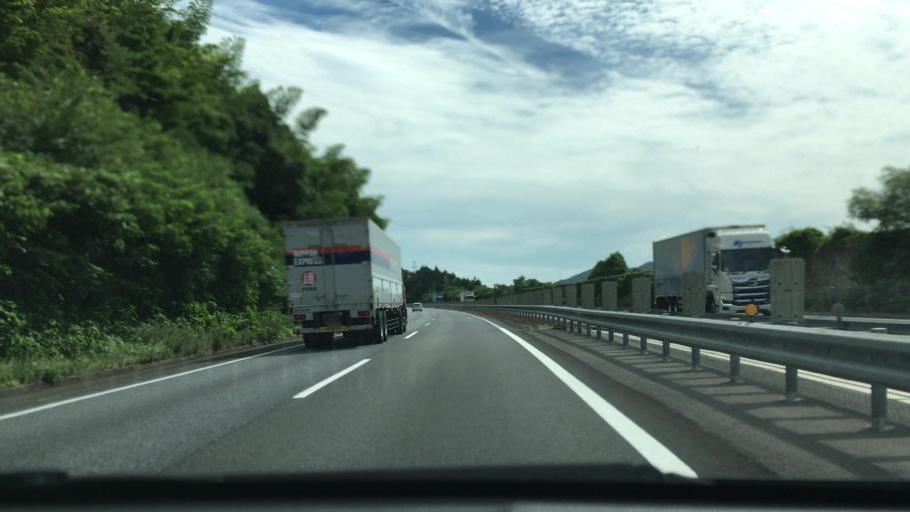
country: JP
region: Yamaguchi
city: Ogori-shimogo
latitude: 34.1298
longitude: 131.4235
